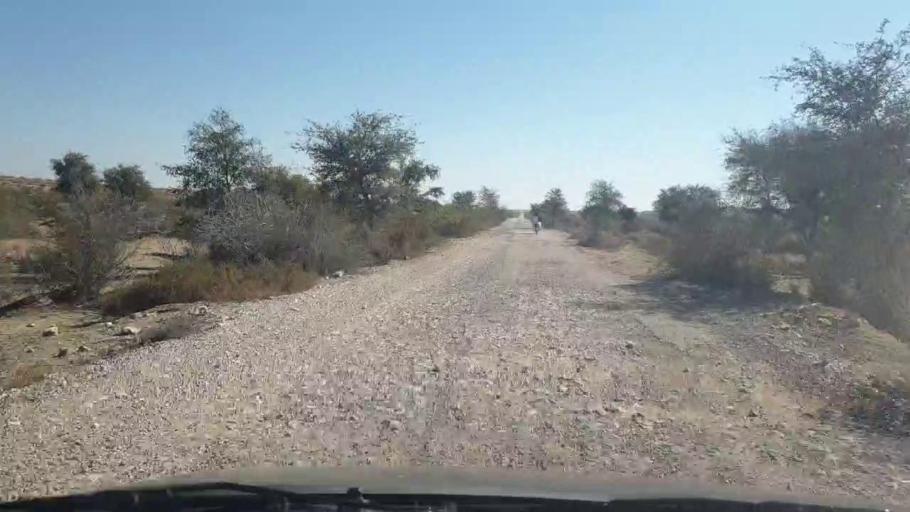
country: PK
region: Sindh
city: Bozdar
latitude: 27.0322
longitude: 68.7019
